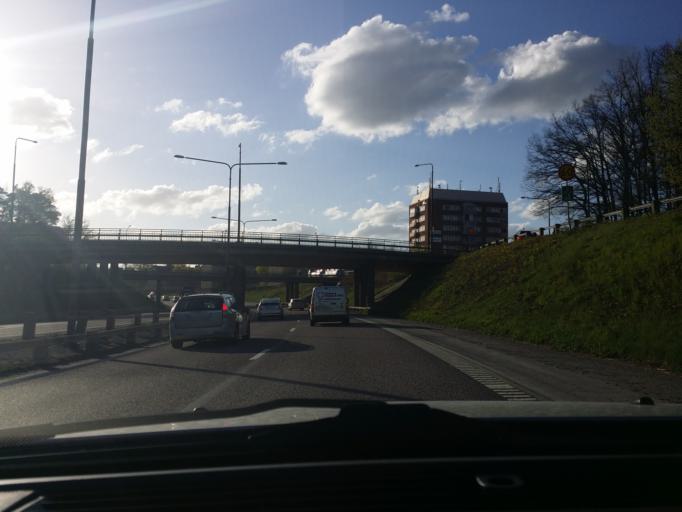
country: SE
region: Vaestmanland
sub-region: Vasteras
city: Vasteras
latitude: 59.6236
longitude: 16.5498
